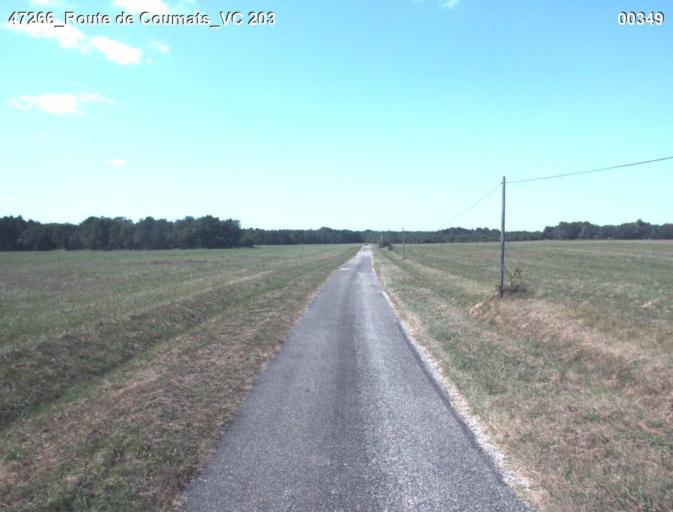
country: FR
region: Aquitaine
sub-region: Departement des Landes
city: Gabarret
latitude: 44.0145
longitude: 0.0895
